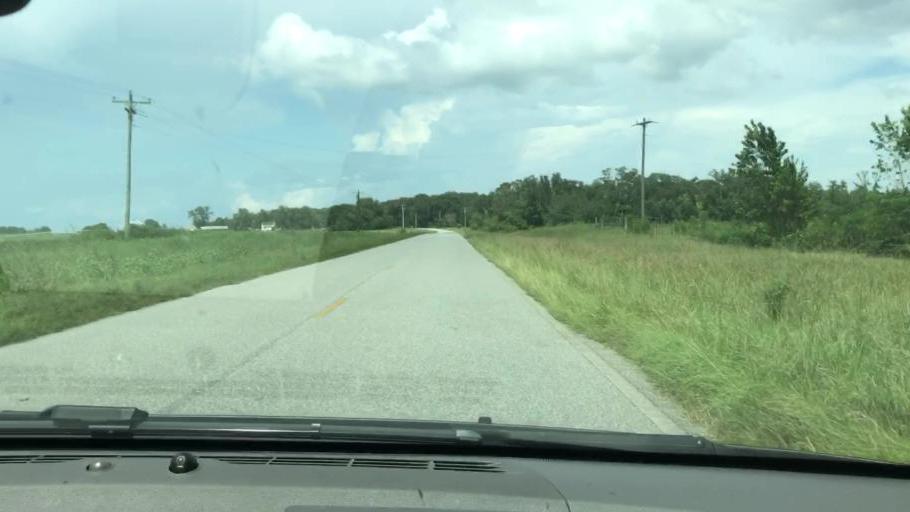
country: US
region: Georgia
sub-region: Seminole County
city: Donalsonville
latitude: 31.0769
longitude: -84.9979
